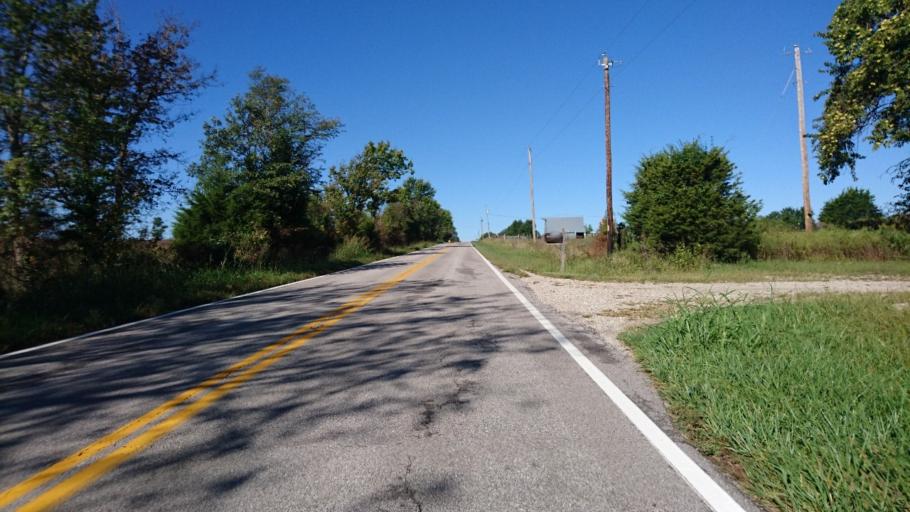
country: US
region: Missouri
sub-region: Greene County
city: Ash Grove
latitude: 37.1938
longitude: -93.6498
